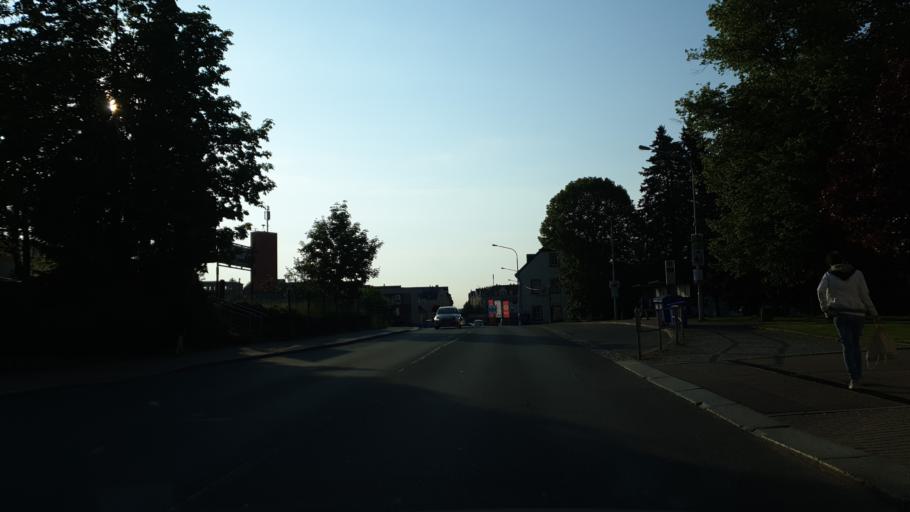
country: DE
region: Saxony
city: Limbach-Oberfrohna
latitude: 50.8585
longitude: 12.7685
